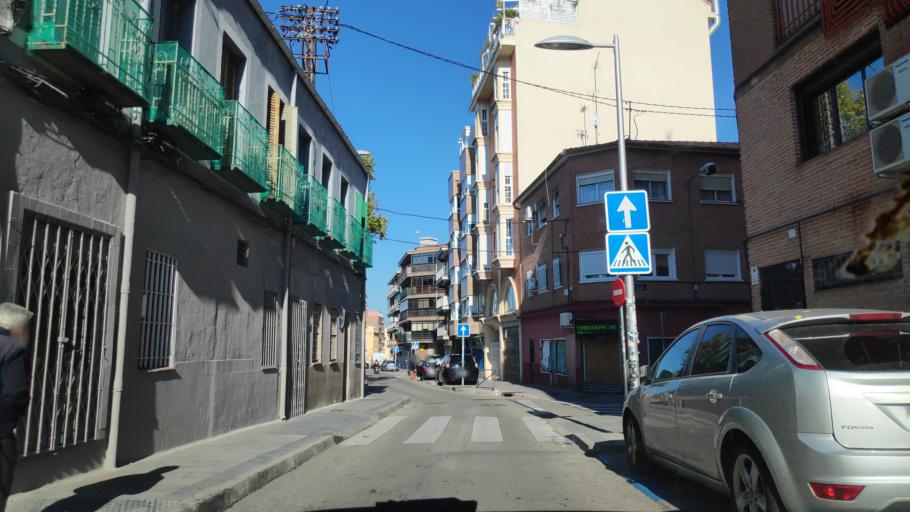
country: ES
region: Madrid
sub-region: Provincia de Madrid
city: Tetuan de las Victorias
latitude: 40.4676
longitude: -3.6975
